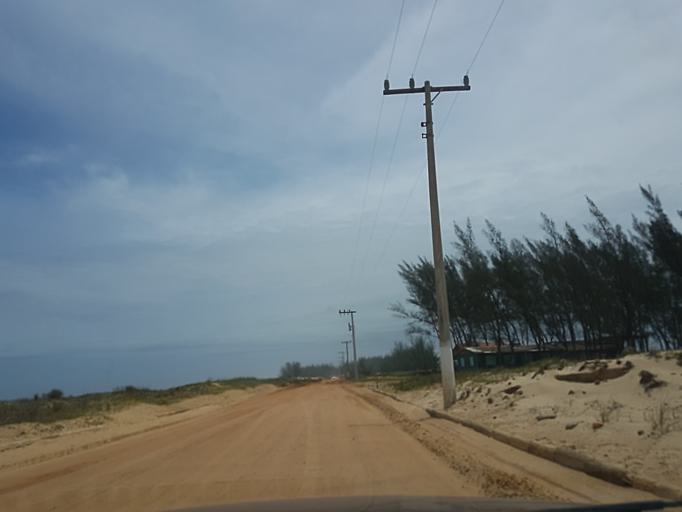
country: BR
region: Santa Catarina
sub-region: Jaguaruna
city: Jaguaruna
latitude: -28.6683
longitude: -48.9702
